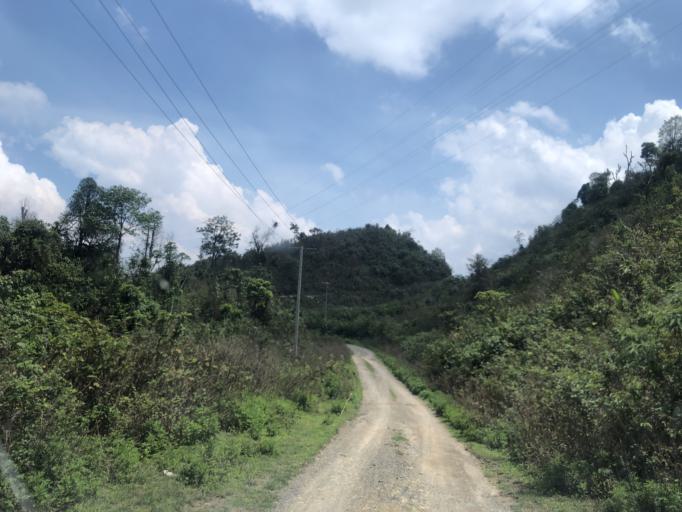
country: LA
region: Phongsali
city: Phongsali
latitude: 21.3916
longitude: 102.1921
